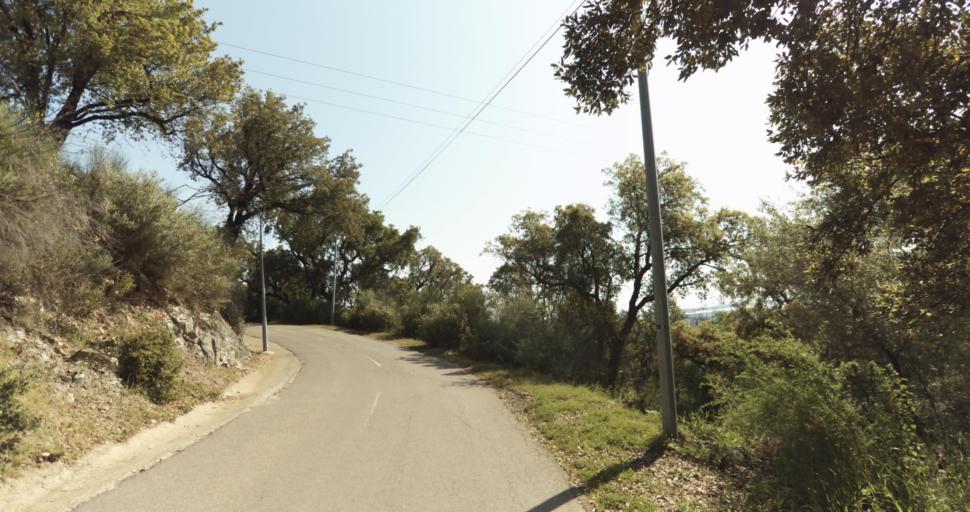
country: FR
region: Corsica
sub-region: Departement de la Haute-Corse
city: Biguglia
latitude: 42.6229
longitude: 9.4202
